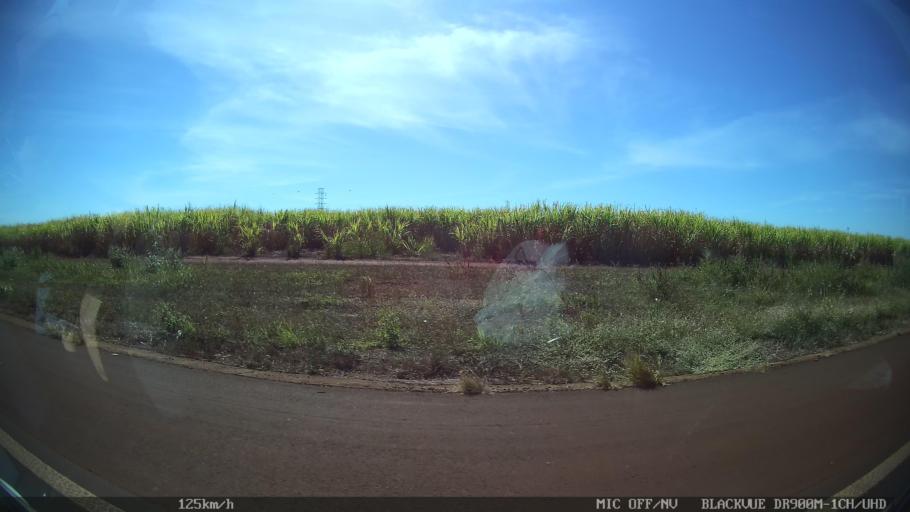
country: BR
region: Sao Paulo
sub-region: Guaira
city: Guaira
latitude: -20.4444
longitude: -48.2748
